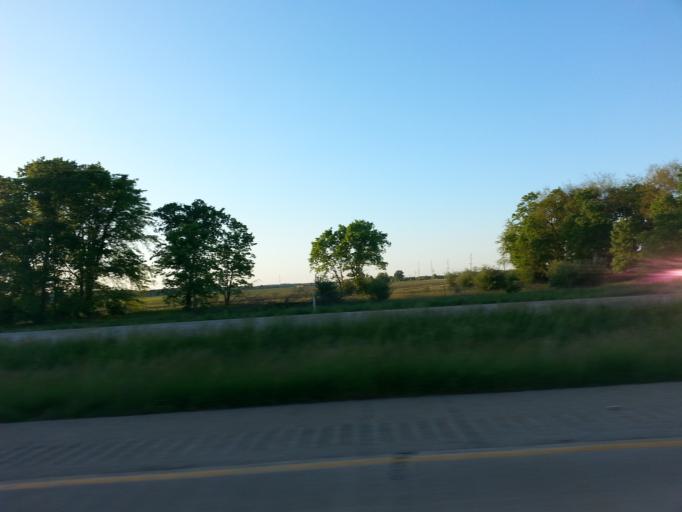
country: US
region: Indiana
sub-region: Fountain County
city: Covington
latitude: 40.1218
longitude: -87.4347
